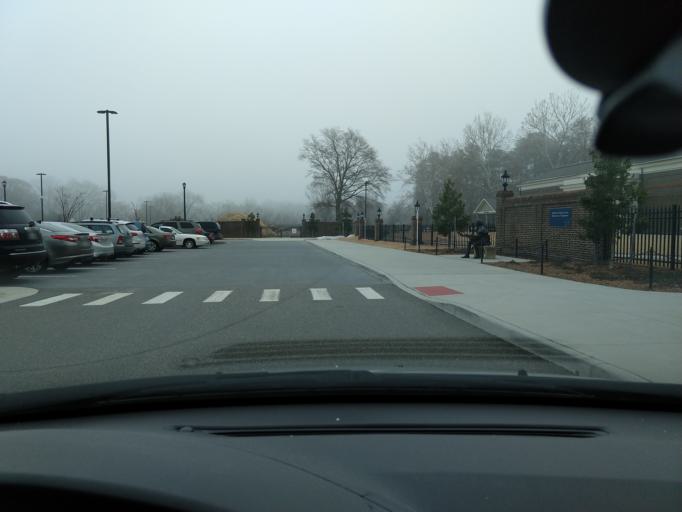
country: US
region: Virginia
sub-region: York County
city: Yorktown
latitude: 37.2390
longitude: -76.5179
